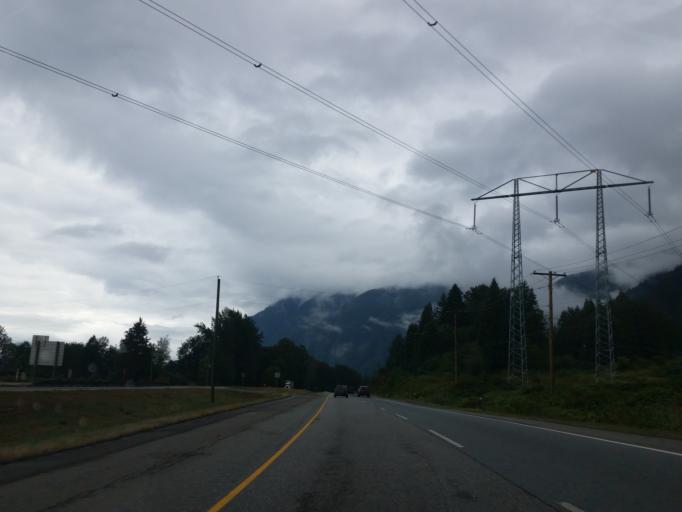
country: CA
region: British Columbia
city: Agassiz
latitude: 49.2078
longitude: -121.7094
